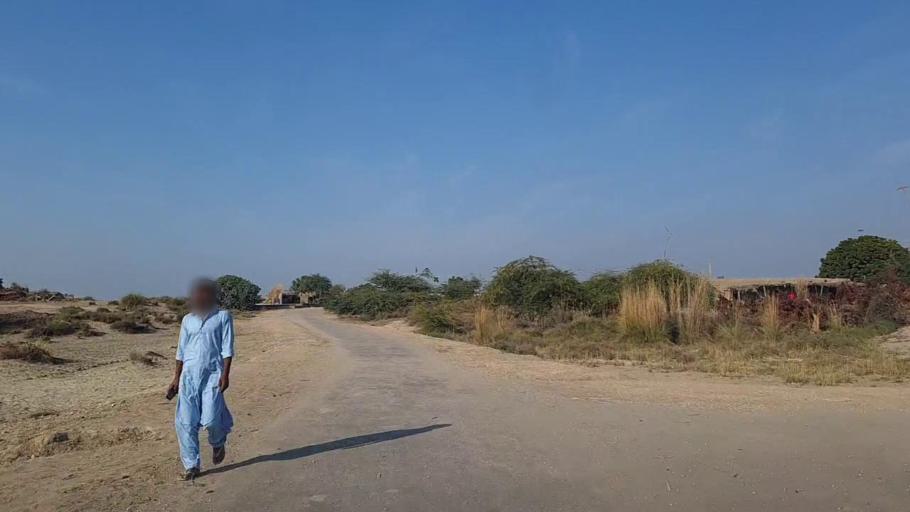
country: PK
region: Sindh
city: Nawabshah
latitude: 26.3733
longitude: 68.4761
